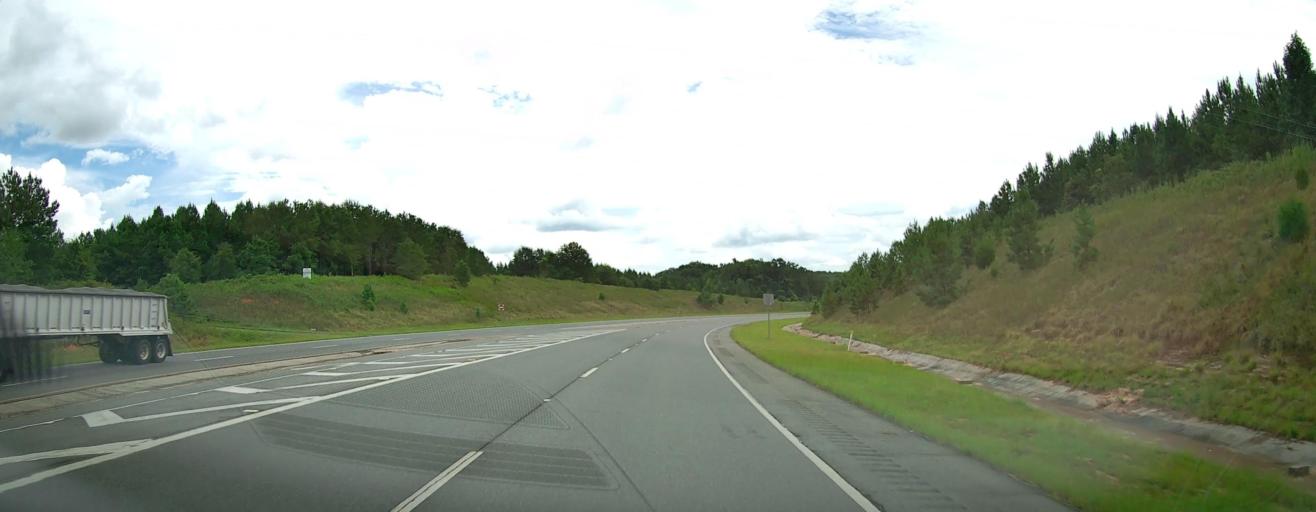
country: US
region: Georgia
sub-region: Schley County
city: Ellaville
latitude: 32.2524
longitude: -84.2988
